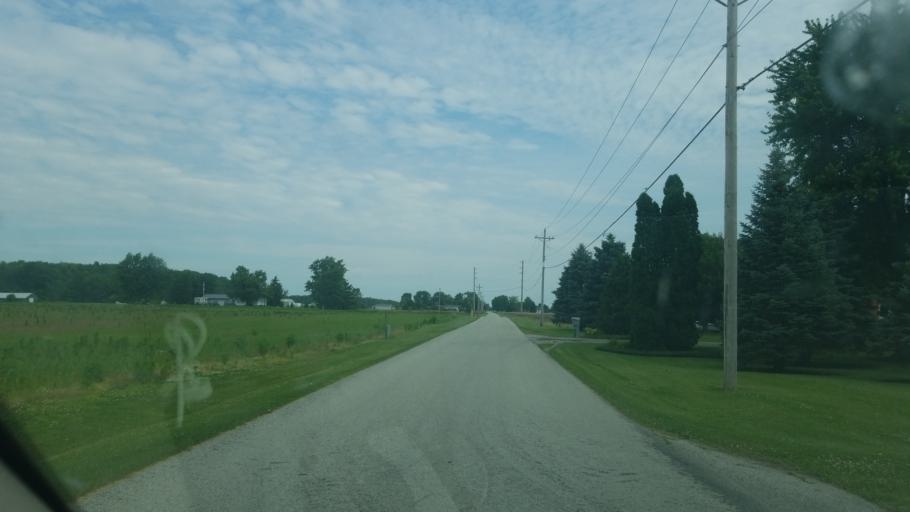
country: US
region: Ohio
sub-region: Seneca County
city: Fostoria
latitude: 41.0599
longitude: -83.4633
